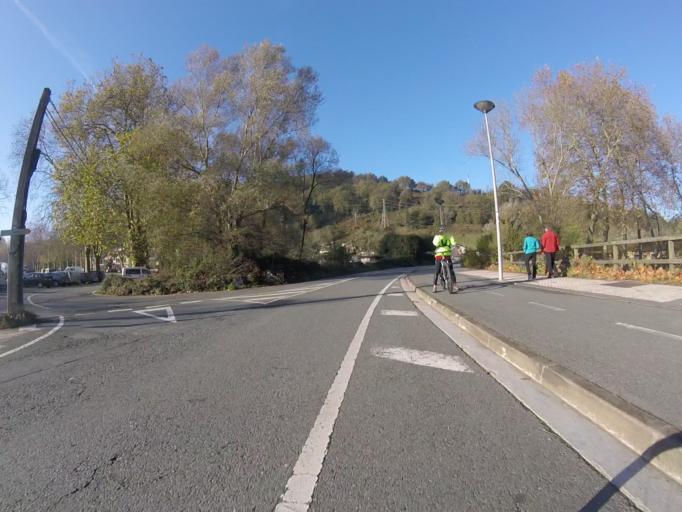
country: ES
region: Basque Country
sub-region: Provincia de Guipuzcoa
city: Lasarte
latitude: 43.2676
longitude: -2.0243
